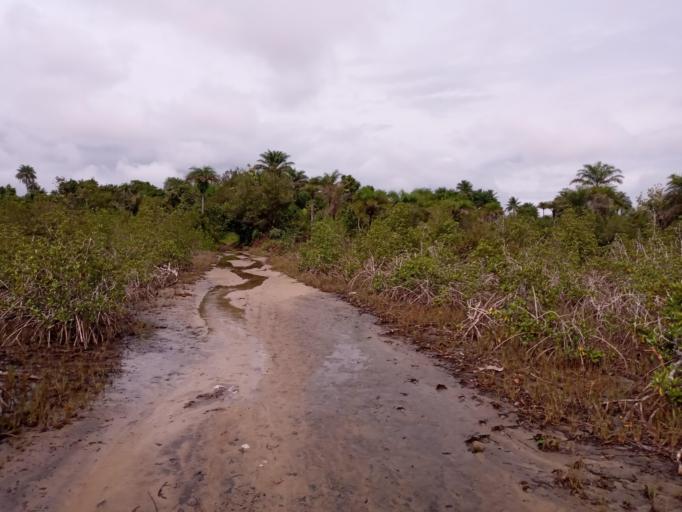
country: SL
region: Southern Province
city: Bonthe
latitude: 7.5135
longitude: -12.5479
